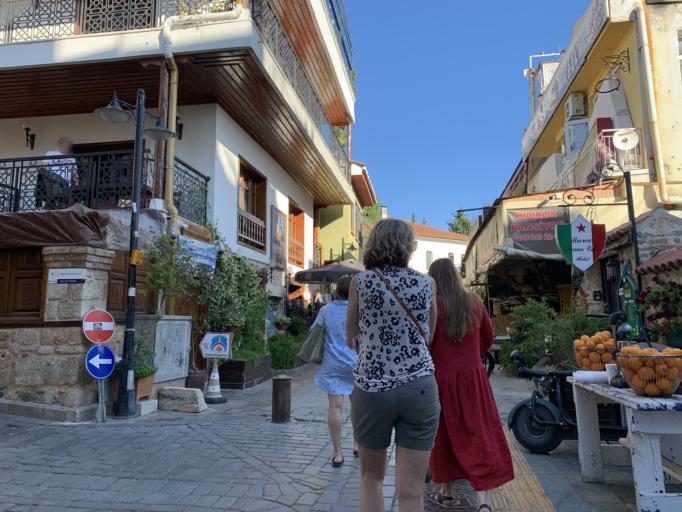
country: TR
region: Antalya
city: Antalya
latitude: 36.8816
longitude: 30.7039
